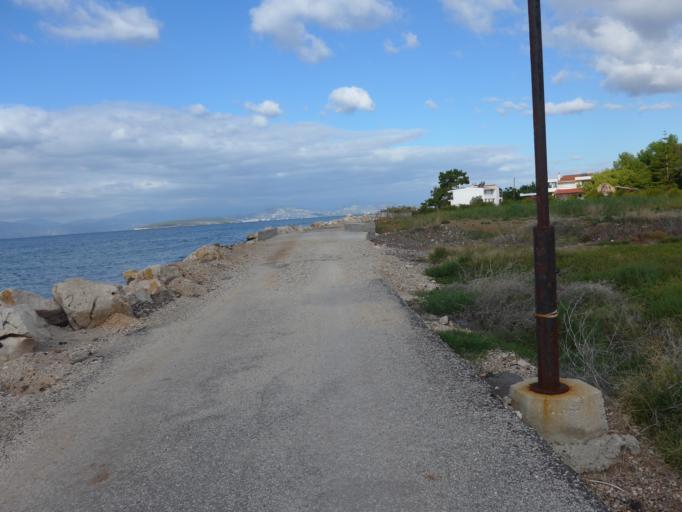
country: GR
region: Peloponnese
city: Asklipieio
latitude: 37.4790
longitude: 22.9977
